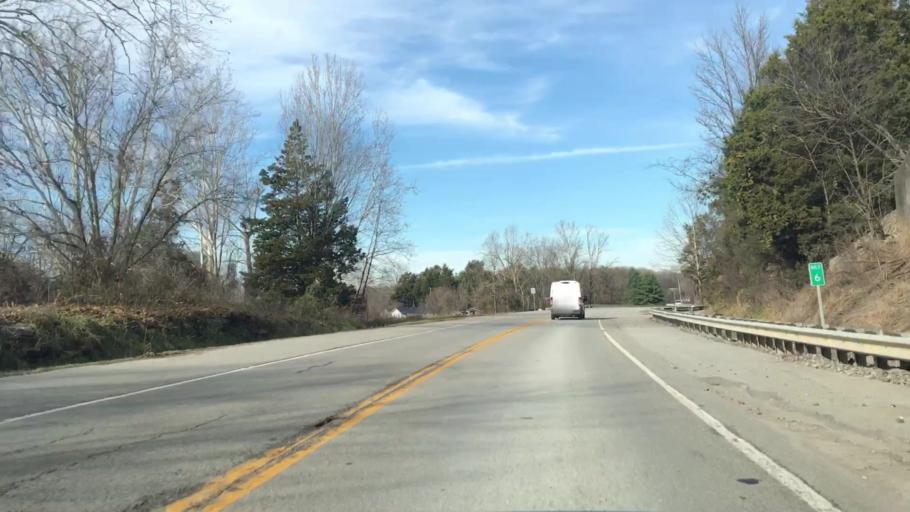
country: US
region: Kentucky
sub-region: Pulaski County
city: Somerset
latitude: 36.9548
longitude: -84.5807
